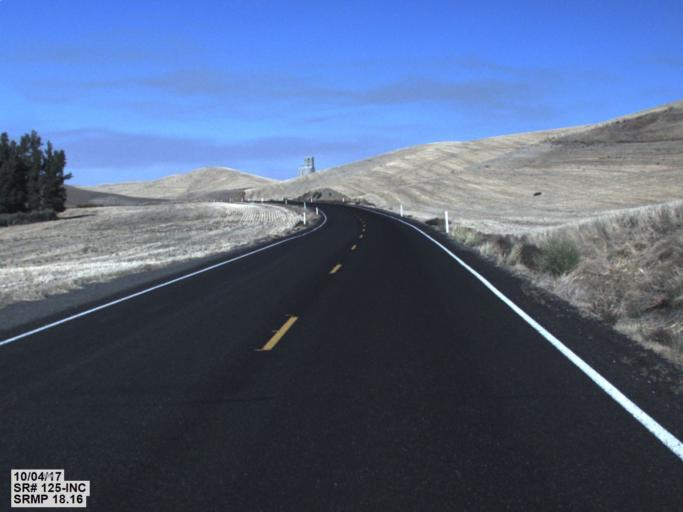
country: US
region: Washington
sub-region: Walla Walla County
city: Walla Walla
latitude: 46.2274
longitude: -118.3832
